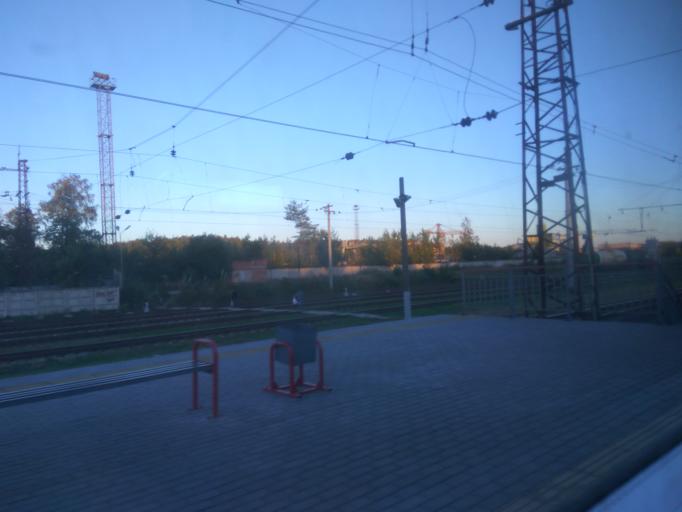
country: RU
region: Moskovskaya
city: Elektrostal'
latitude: 55.7685
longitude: 38.4689
